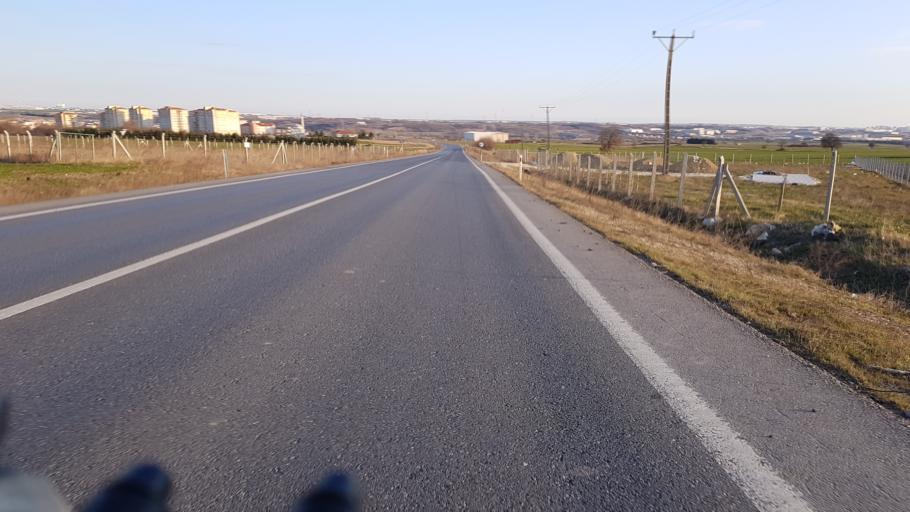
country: TR
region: Tekirdag
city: Velimese
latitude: 41.2586
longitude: 27.8599
